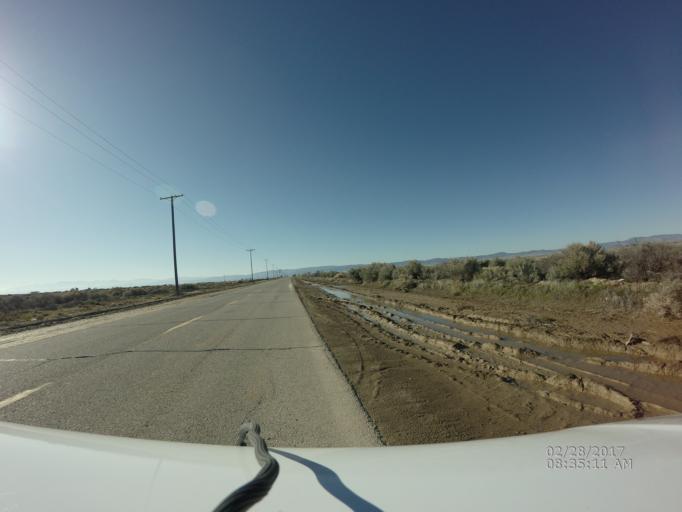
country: US
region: California
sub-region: Kern County
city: Rosamond
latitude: 34.8098
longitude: -118.2377
